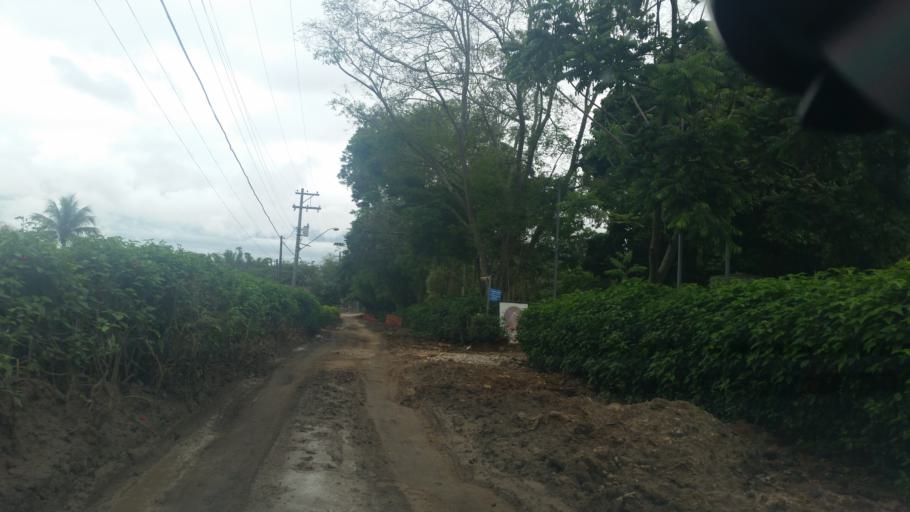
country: BR
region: Sao Paulo
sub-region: Taubate
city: Taubate
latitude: -23.0252
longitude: -45.6298
